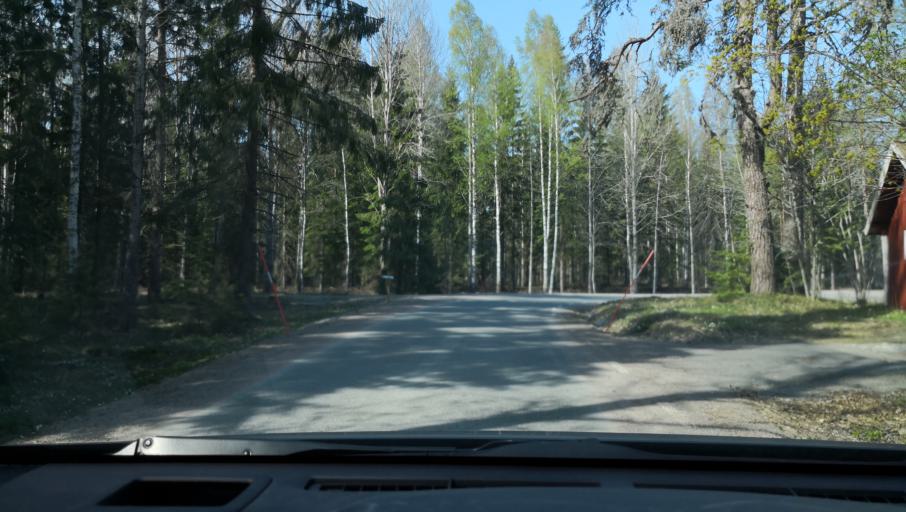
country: SE
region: Vaestmanland
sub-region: Sala Kommun
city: Sala
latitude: 60.0086
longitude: 16.6761
